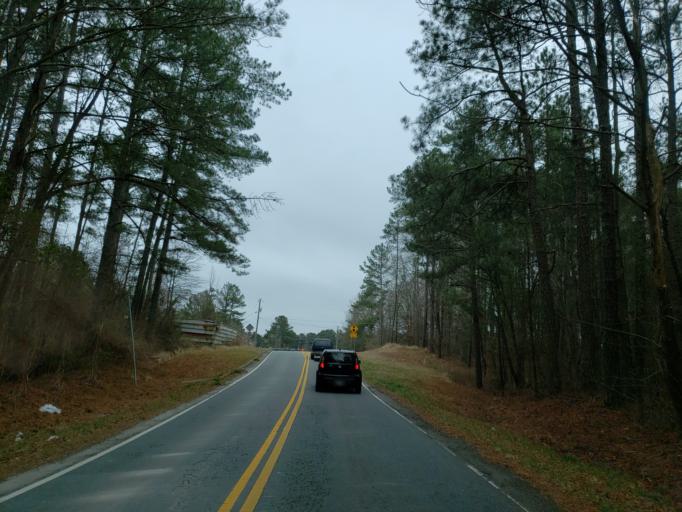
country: US
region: Georgia
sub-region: Paulding County
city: Hiram
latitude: 33.9056
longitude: -84.7259
